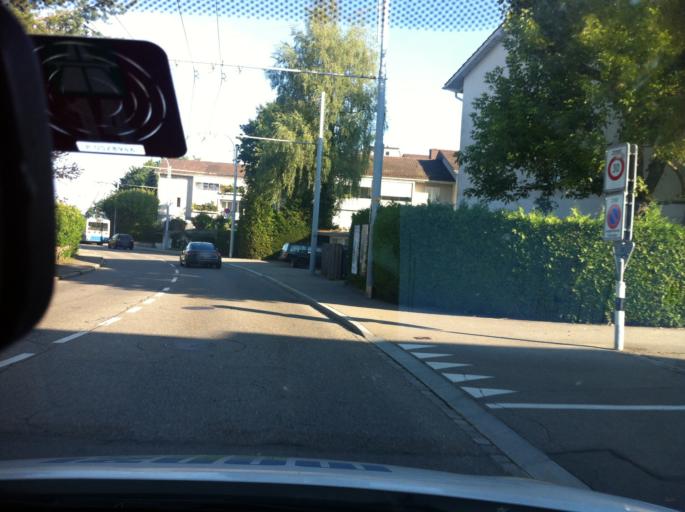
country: CH
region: Zurich
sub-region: Bezirk Zuerich
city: Zuerich (Kreis 7) / Witikon
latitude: 47.3570
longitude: 8.5977
